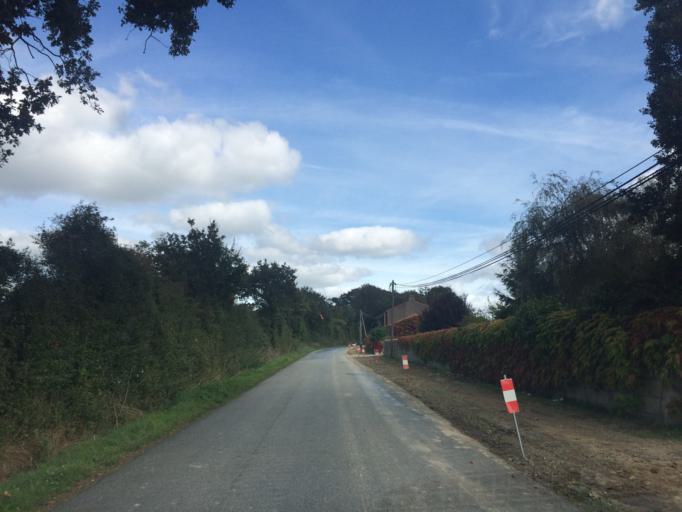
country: FR
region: Pays de la Loire
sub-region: Departement de la Loire-Atlantique
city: Chemere
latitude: 47.1063
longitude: -1.8972
